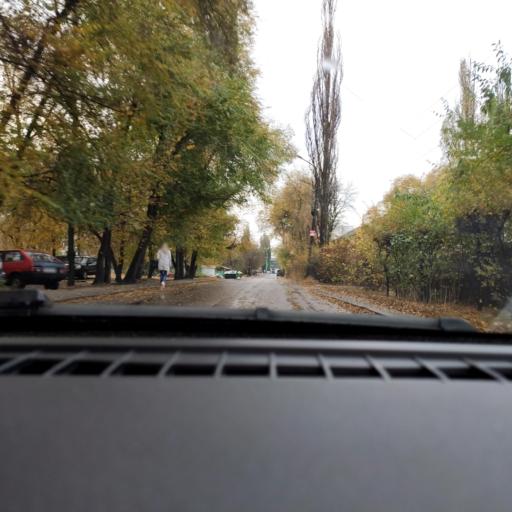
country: RU
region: Voronezj
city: Voronezh
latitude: 51.6609
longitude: 39.2833
